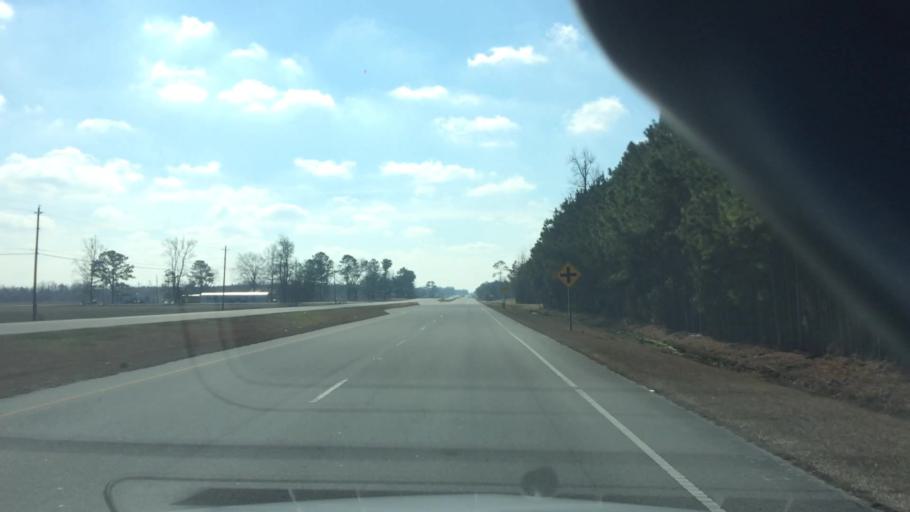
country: US
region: North Carolina
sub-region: Duplin County
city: Beulaville
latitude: 35.1129
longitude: -77.7181
